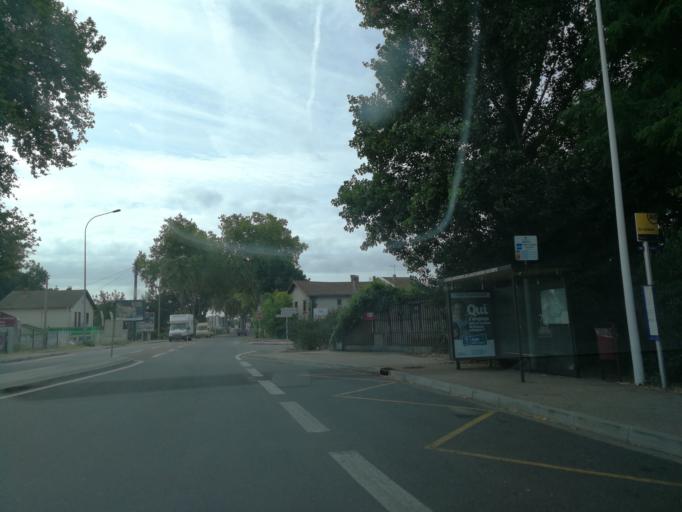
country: FR
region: Midi-Pyrenees
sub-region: Departement de la Haute-Garonne
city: Saint-Alban
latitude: 43.6766
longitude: 1.4085
